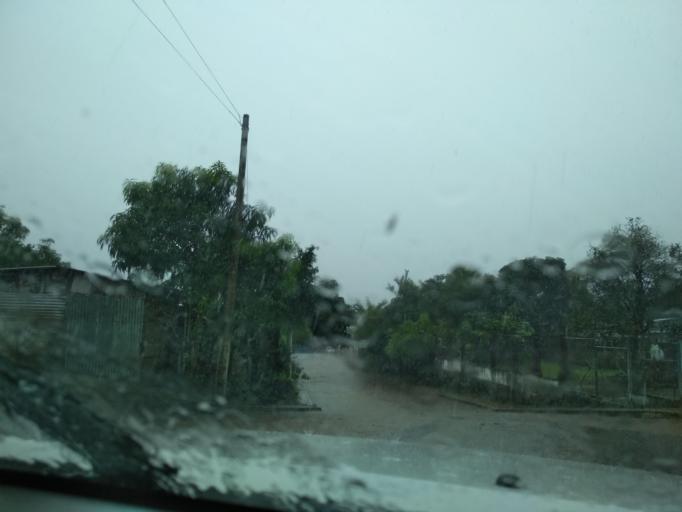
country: MX
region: Veracruz
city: Santiago Tuxtla
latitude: 18.4728
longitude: -95.3046
